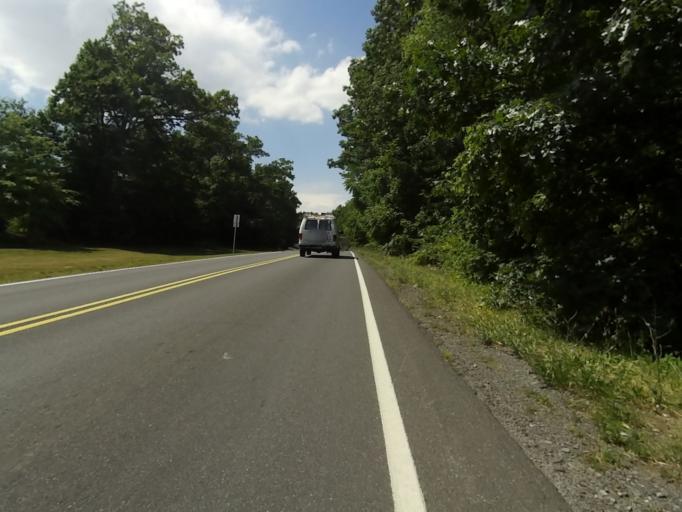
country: US
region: Pennsylvania
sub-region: Centre County
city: Park Forest Village
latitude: 40.7917
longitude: -77.9086
